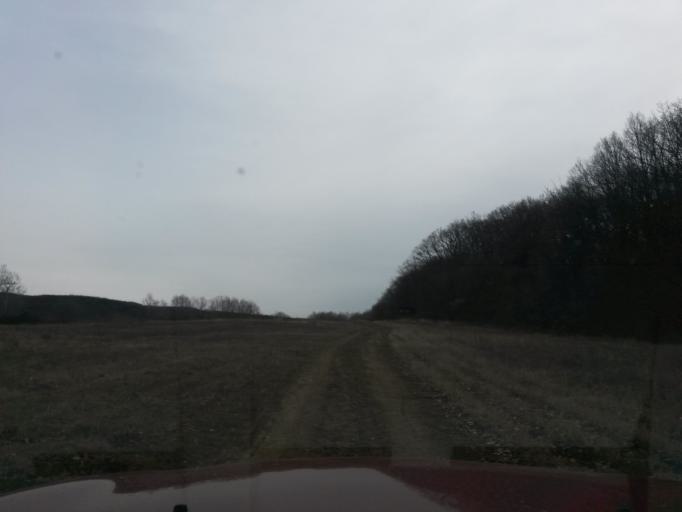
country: HU
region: Borsod-Abauj-Zemplen
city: Gonc
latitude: 48.5779
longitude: 21.3797
